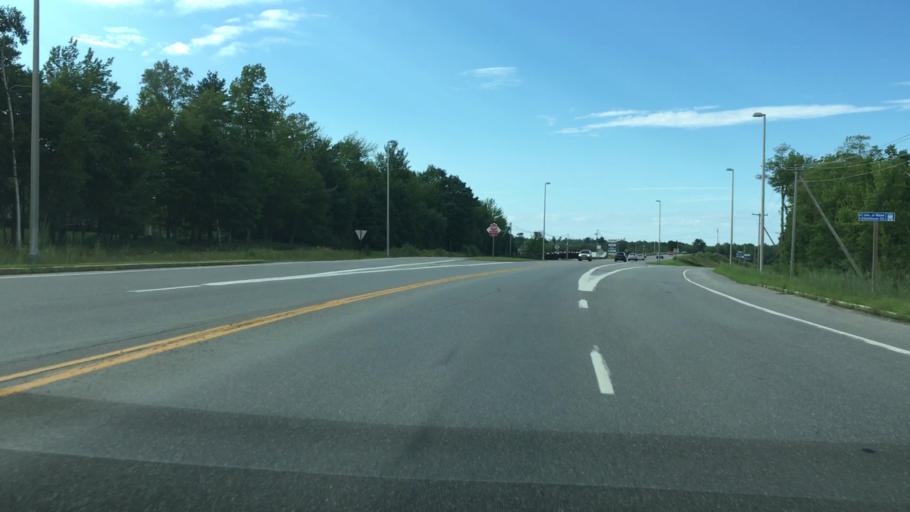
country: US
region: Maine
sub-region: Waldo County
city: Belfast
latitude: 44.4192
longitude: -69.0199
